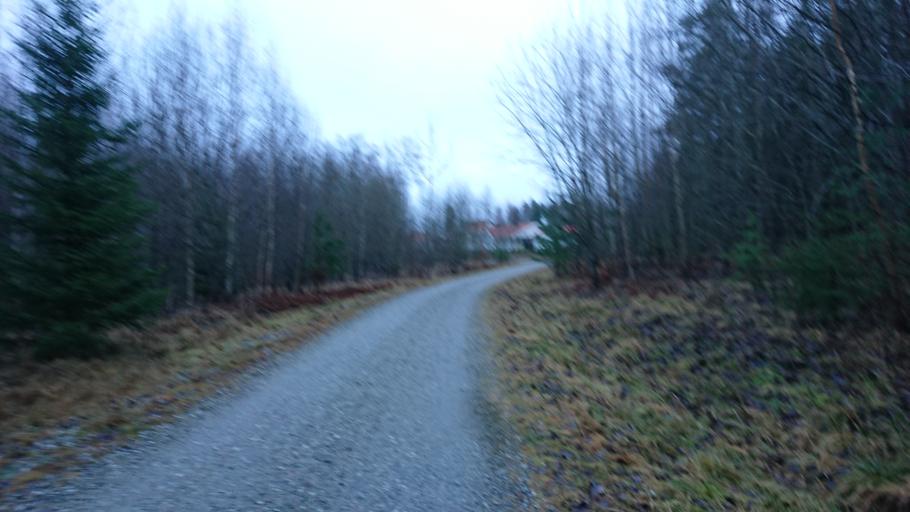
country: SE
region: Soedermanland
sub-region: Strangnas Kommun
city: Stallarholmen
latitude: 59.3664
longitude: 17.1826
